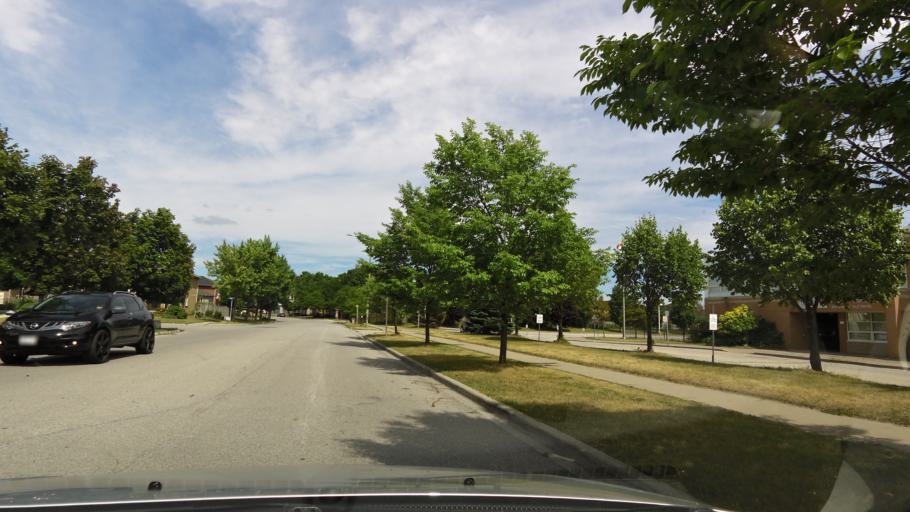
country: CA
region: Ontario
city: Mississauga
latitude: 43.6192
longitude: -79.6610
